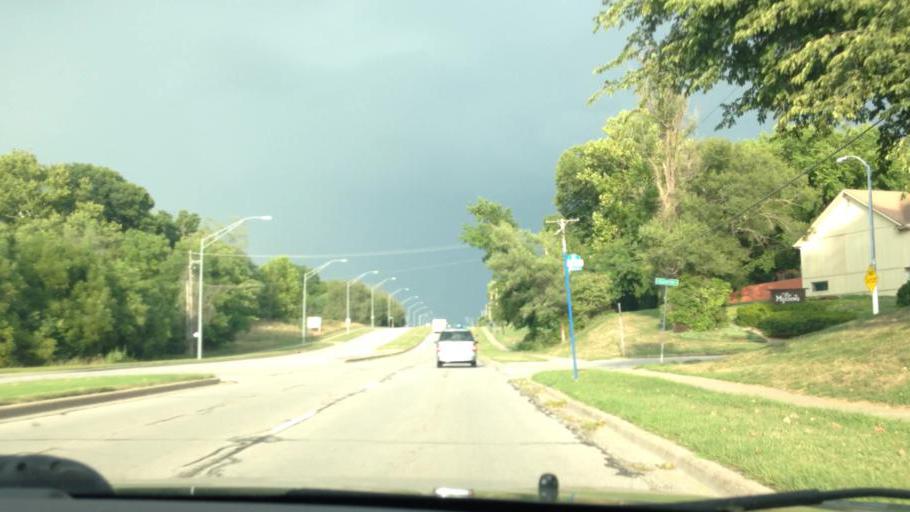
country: US
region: Missouri
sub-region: Platte County
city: Riverside
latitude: 39.2463
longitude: -94.6141
